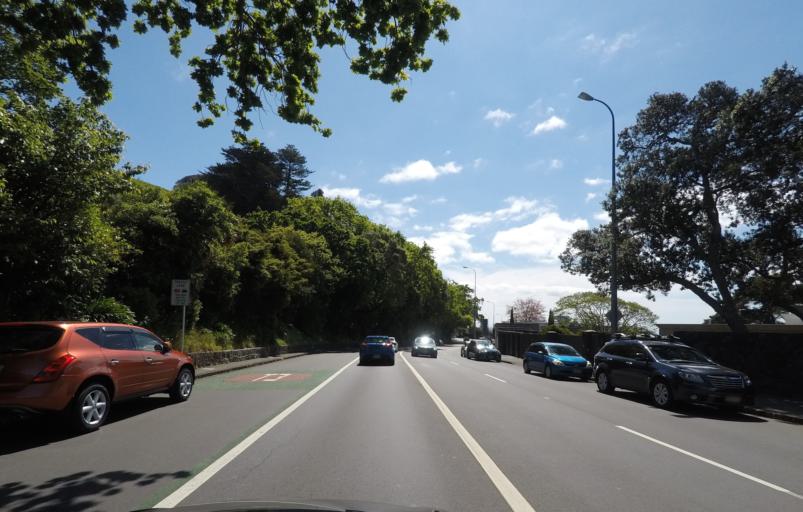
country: NZ
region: Auckland
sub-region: Auckland
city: Auckland
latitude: -36.8785
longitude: 174.7898
